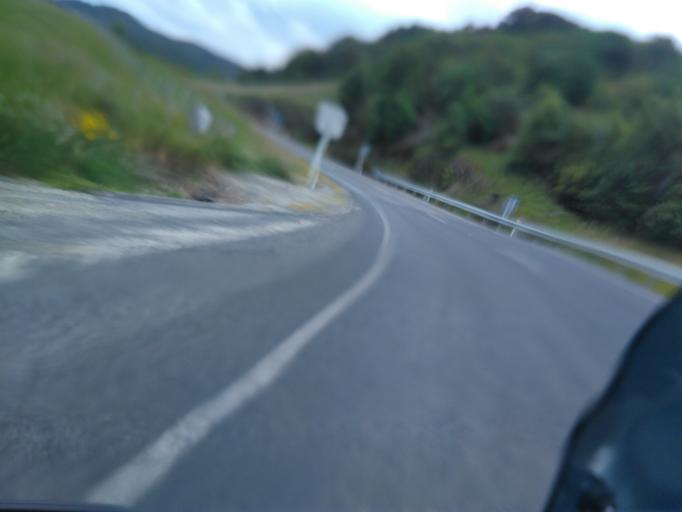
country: NZ
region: Bay of Plenty
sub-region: Opotiki District
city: Opotiki
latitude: -38.3484
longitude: 177.4481
